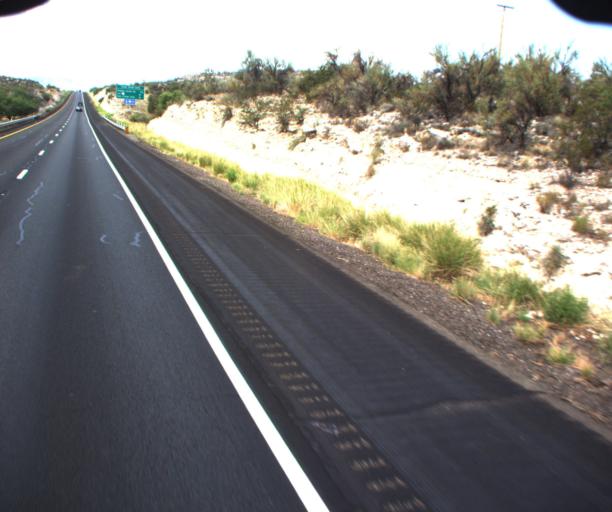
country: US
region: Arizona
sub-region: Yavapai County
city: Lake Montezuma
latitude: 34.6264
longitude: -111.8393
